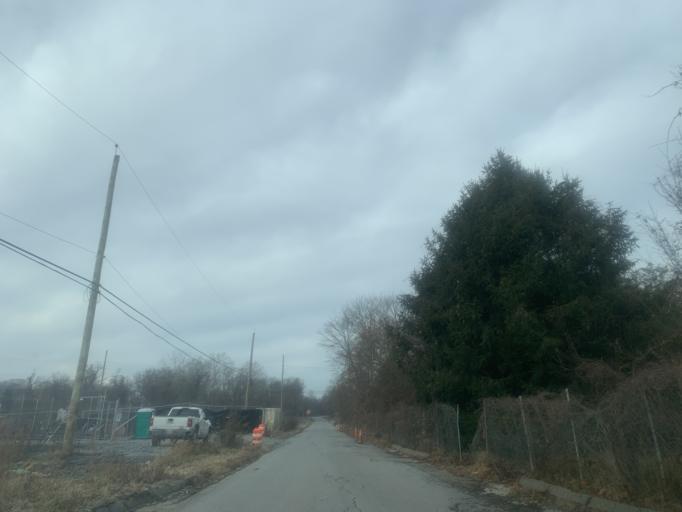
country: US
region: Maryland
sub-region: Prince George's County
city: Forestville
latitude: 38.8310
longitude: -76.8528
